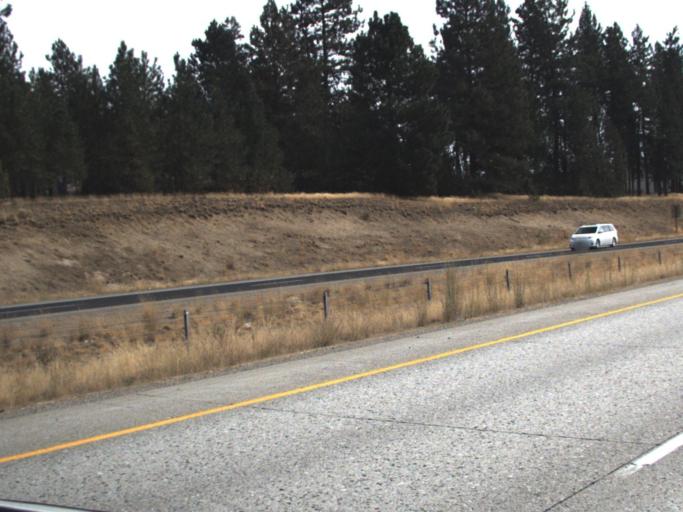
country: US
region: Washington
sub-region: Spokane County
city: Fairwood
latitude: 47.8135
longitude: -117.4085
